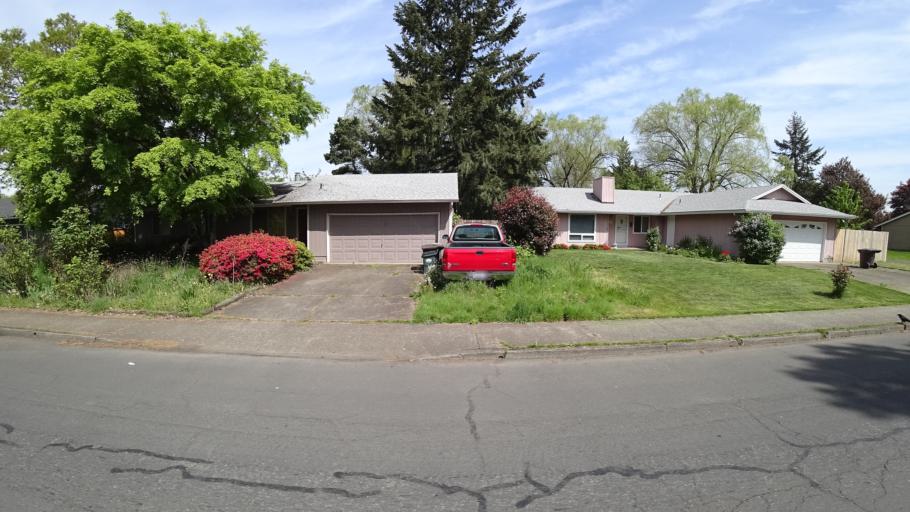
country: US
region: Oregon
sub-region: Washington County
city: Hillsboro
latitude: 45.5279
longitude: -122.9554
